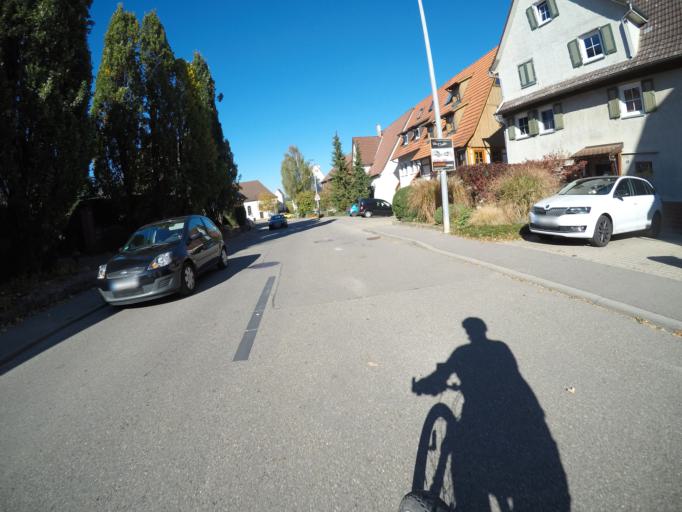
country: DE
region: Baden-Wuerttemberg
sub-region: Regierungsbezirk Stuttgart
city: Herrenberg
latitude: 48.5823
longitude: 8.8407
